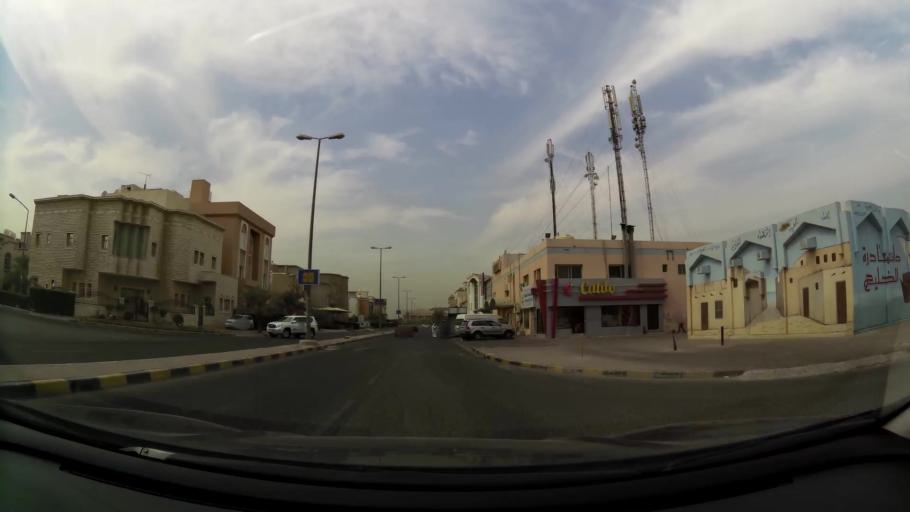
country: KW
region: Mubarak al Kabir
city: Sabah as Salim
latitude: 29.2679
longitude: 48.0257
